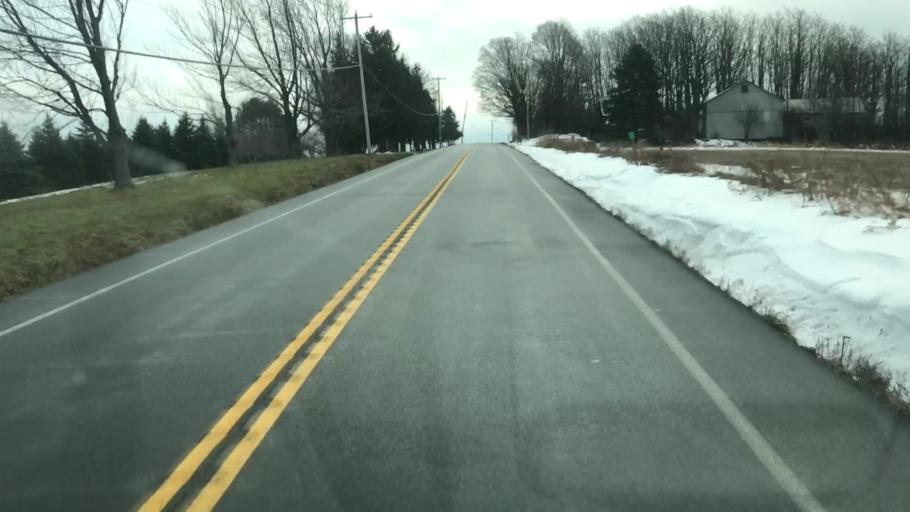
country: US
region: New York
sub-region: Onondaga County
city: Skaneateles
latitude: 42.8471
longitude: -76.3897
